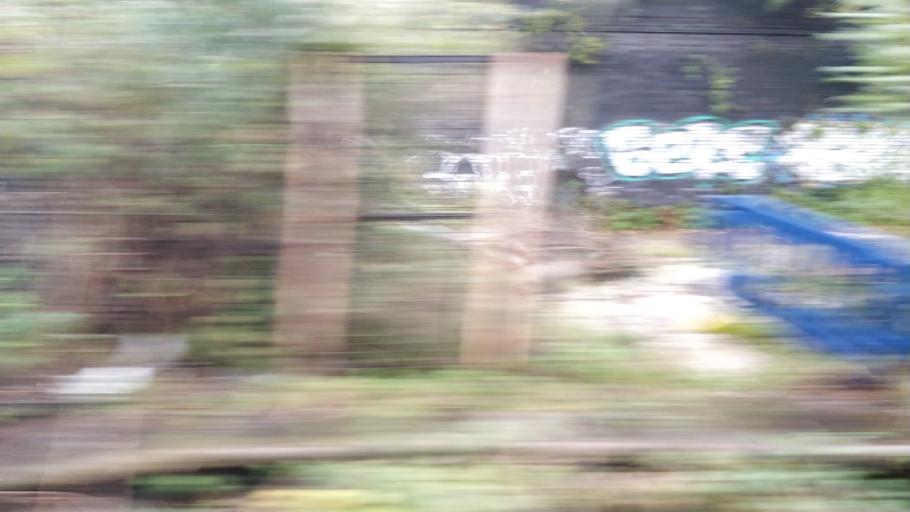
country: GB
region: England
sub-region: City and Borough of Salford
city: Salford
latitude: 53.4925
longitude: -2.2838
